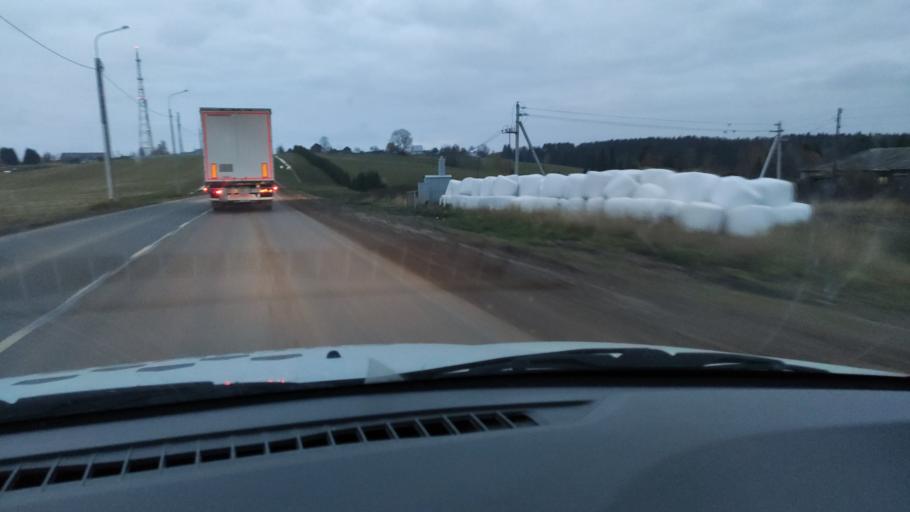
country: RU
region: Kirov
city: Kostino
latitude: 58.8510
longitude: 53.2756
